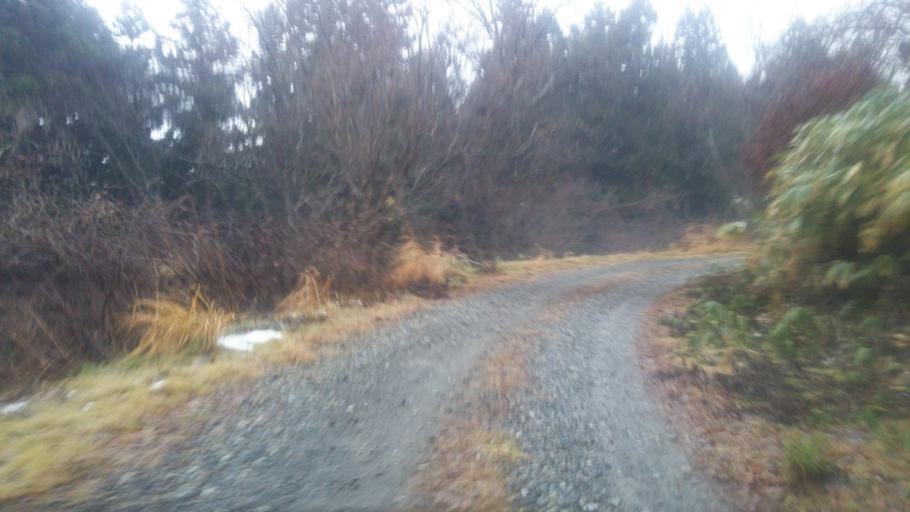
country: JP
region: Fukushima
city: Kitakata
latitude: 37.5740
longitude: 139.9801
